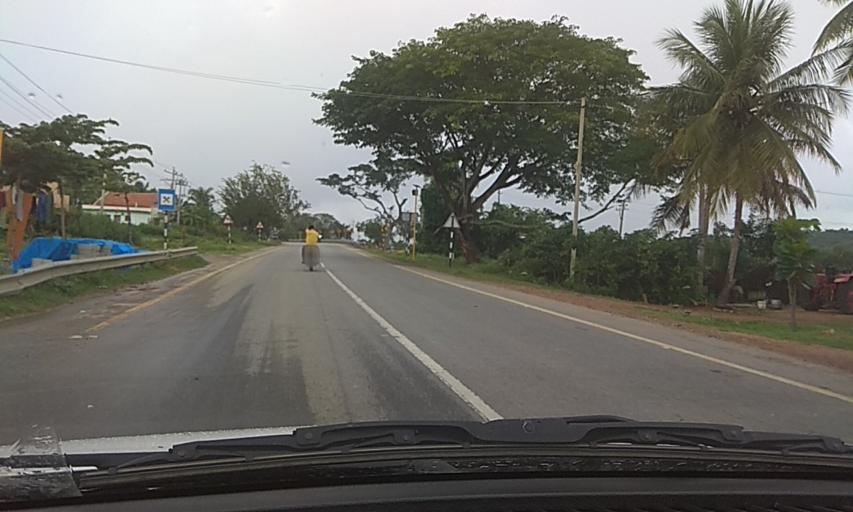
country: IN
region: Karnataka
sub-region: Mandya
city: Maddur
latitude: 12.7885
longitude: 77.0479
